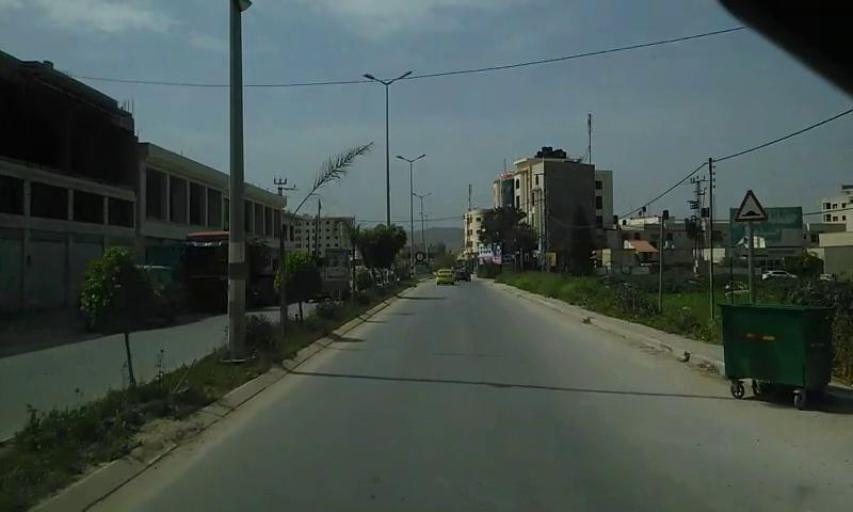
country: PS
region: West Bank
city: Janin
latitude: 32.4684
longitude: 35.2948
